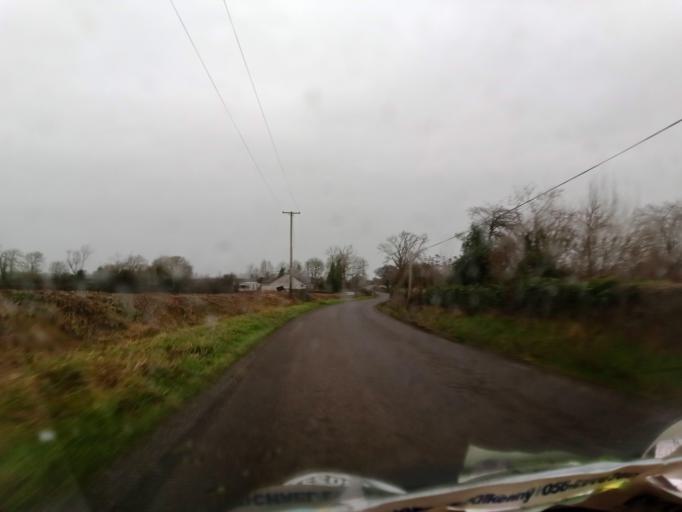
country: IE
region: Munster
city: Fethard
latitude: 52.5570
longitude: -7.7651
